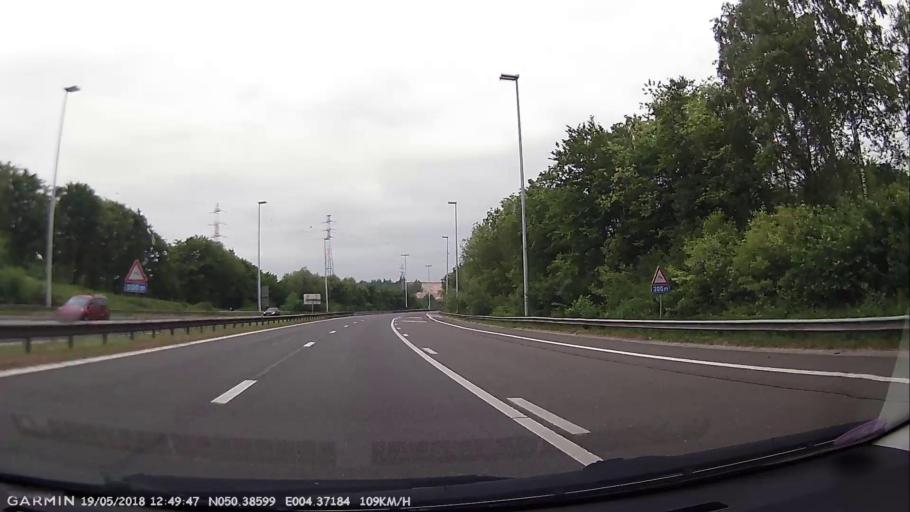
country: BE
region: Wallonia
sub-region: Province du Hainaut
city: Charleroi
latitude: 50.3863
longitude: 4.3715
